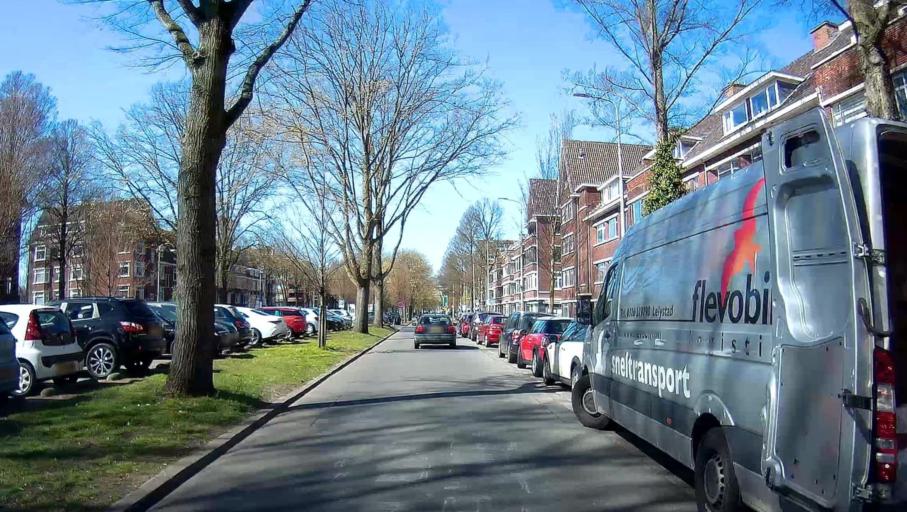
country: NL
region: South Holland
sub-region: Gemeente Den Haag
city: The Hague
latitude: 52.0641
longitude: 4.2556
